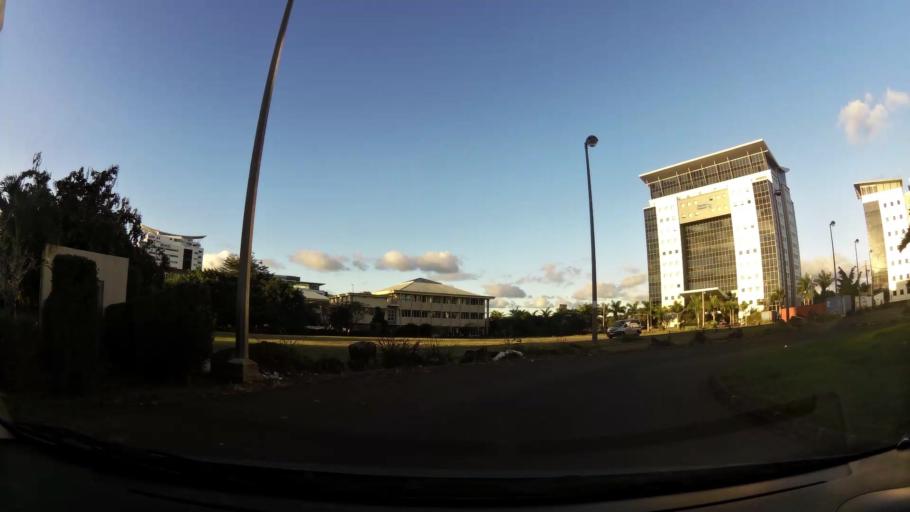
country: MU
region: Plaines Wilhems
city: Ebene
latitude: -20.2432
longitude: 57.4948
